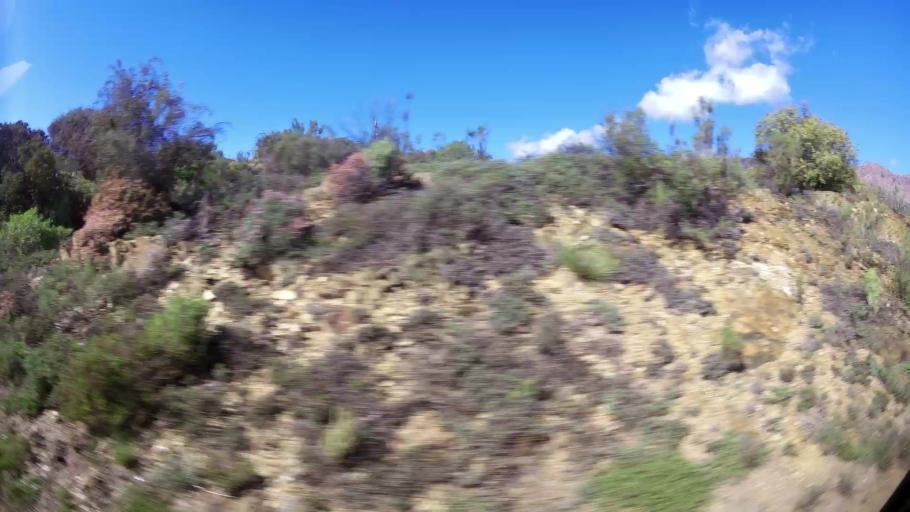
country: ZA
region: Western Cape
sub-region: Cape Winelands District Municipality
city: Ashton
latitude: -33.7895
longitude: 20.1322
